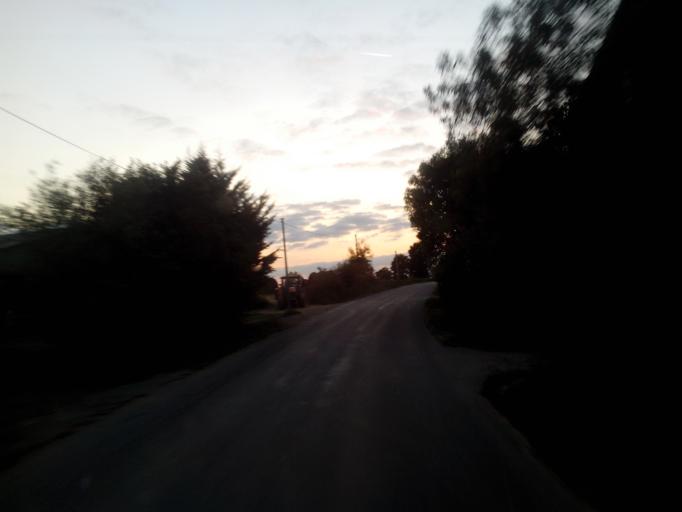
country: FR
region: Brittany
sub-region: Departement d'Ille-et-Vilaine
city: Montfort-sur-Meu
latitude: 48.1511
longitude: -1.9587
